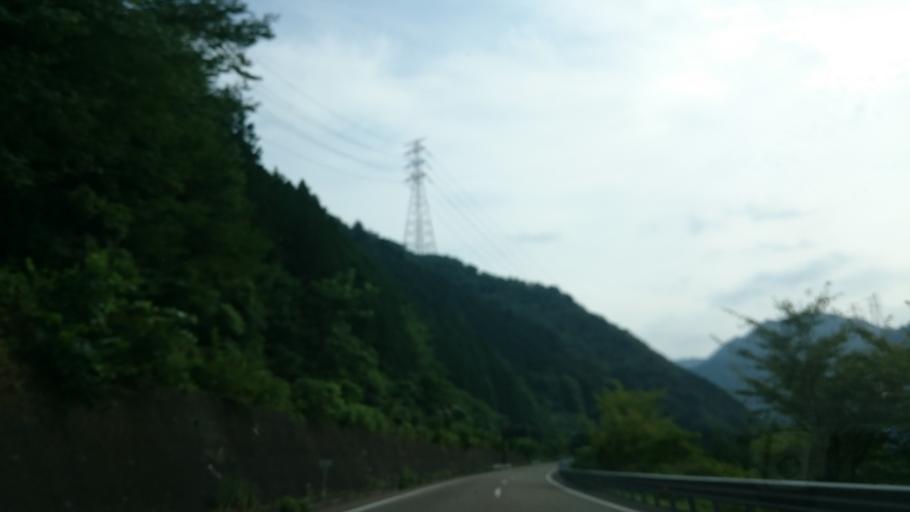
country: JP
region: Gifu
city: Mino
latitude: 35.6215
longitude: 136.9519
